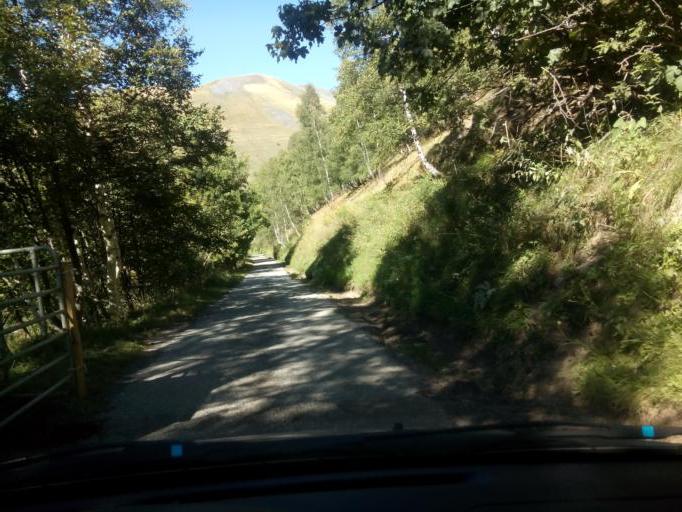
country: FR
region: Rhone-Alpes
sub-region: Departement de l'Isere
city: Mont-de-Lans
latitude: 45.0732
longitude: 6.1796
